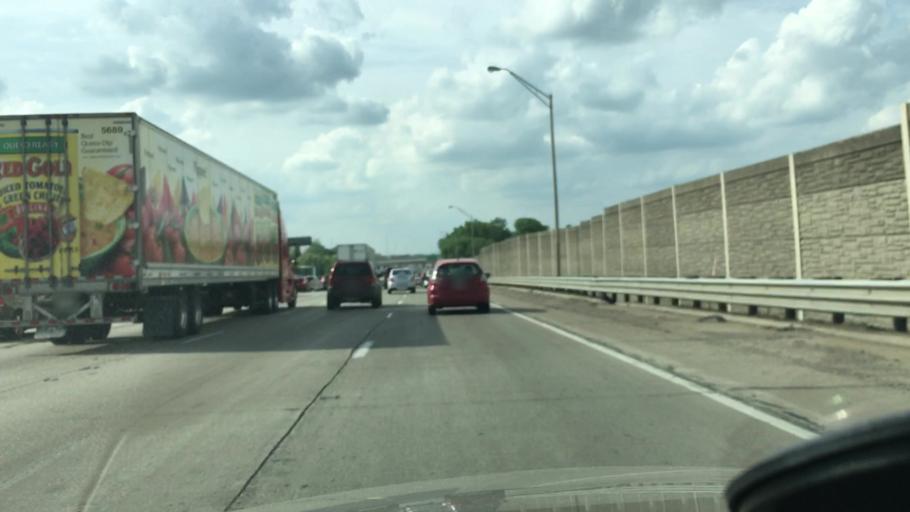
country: US
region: Indiana
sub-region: Marion County
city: Lawrence
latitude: 39.8358
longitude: -86.0376
